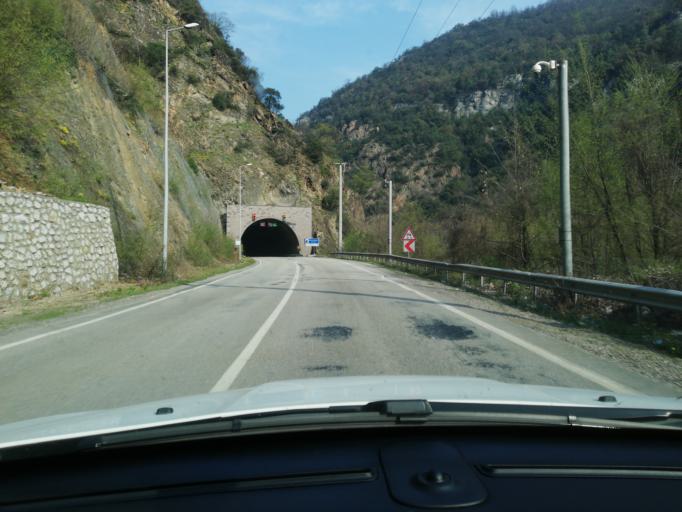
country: TR
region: Karabuk
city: Yenice
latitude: 41.1604
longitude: 32.4591
